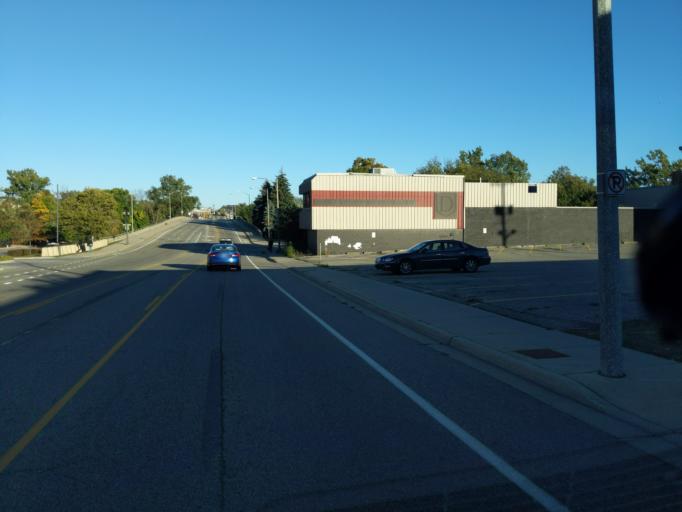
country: US
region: Michigan
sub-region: Ingham County
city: Lansing
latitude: 42.7299
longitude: -84.5502
